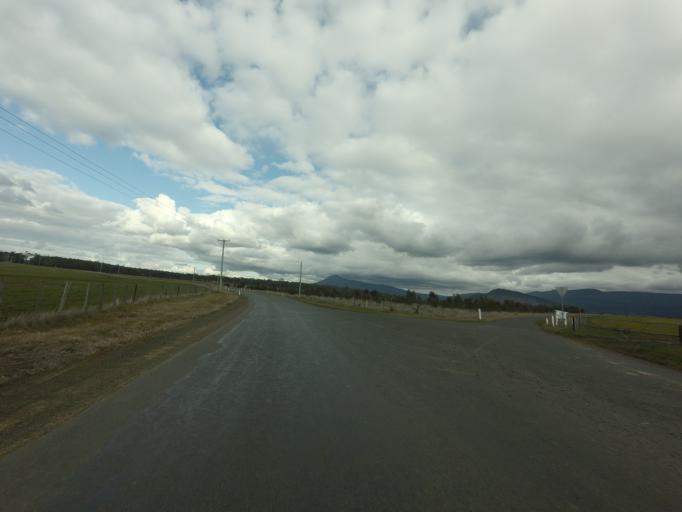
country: AU
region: Tasmania
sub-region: Northern Midlands
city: Longford
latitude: -41.7940
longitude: 147.1139
